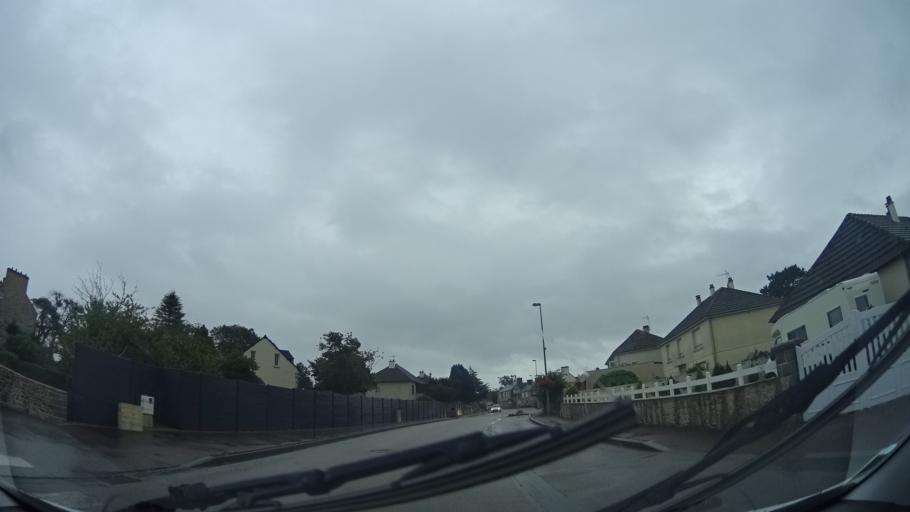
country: FR
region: Lower Normandy
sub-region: Departement de la Manche
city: Urville-Nacqueville
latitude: 49.5960
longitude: -1.7748
